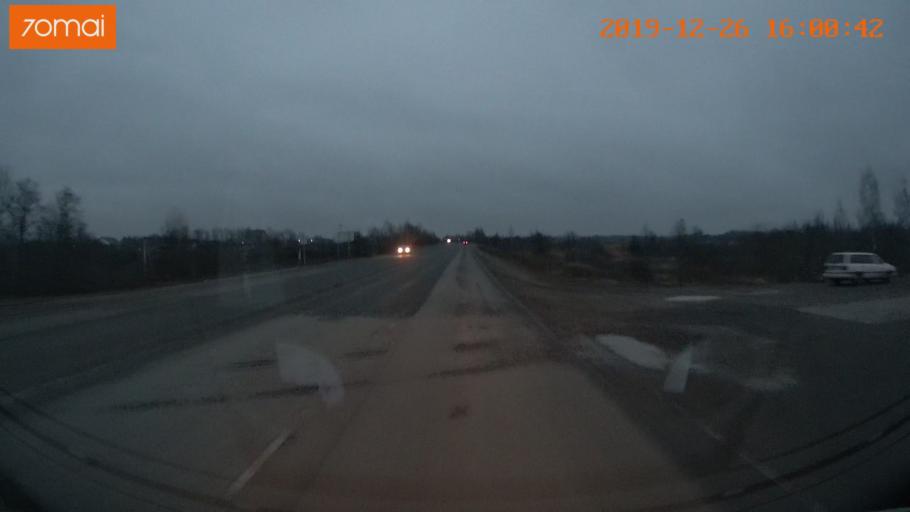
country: RU
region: Jaroslavl
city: Rybinsk
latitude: 58.0213
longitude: 38.8061
